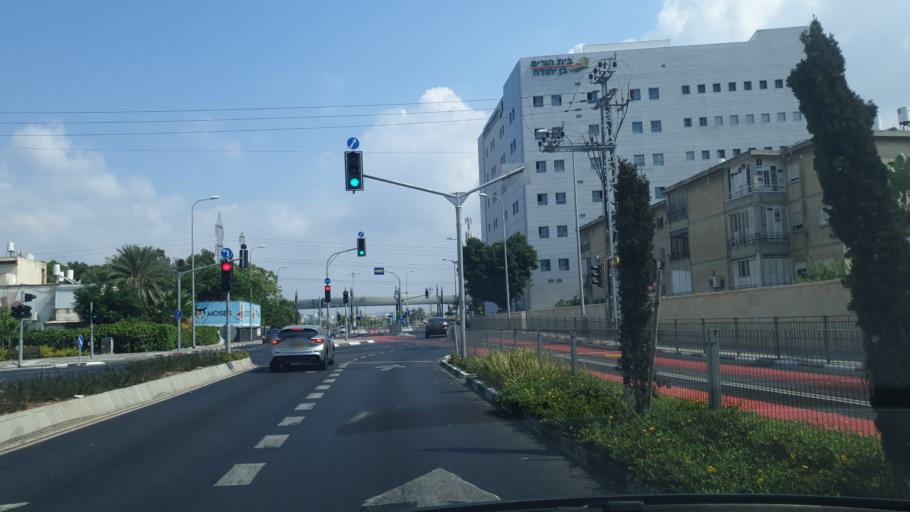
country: IL
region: Haifa
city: Qiryat Bialik
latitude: 32.8169
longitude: 35.0786
